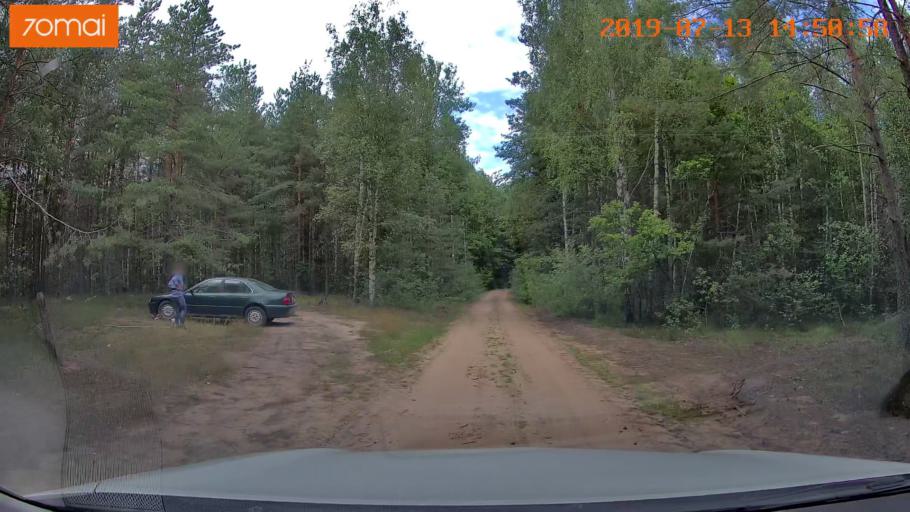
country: BY
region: Mogilev
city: Asipovichy
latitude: 53.2097
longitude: 28.7500
